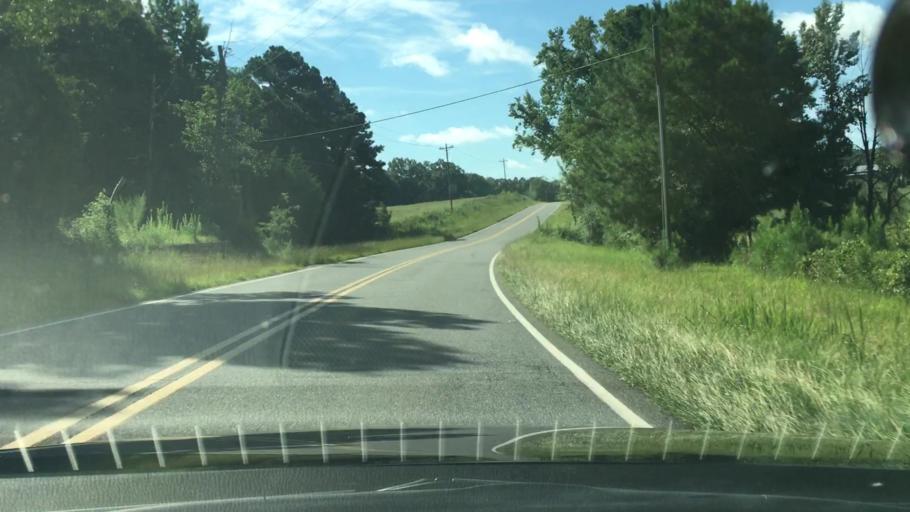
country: US
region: Georgia
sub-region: Putnam County
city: Jefferson
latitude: 33.4522
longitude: -83.2998
